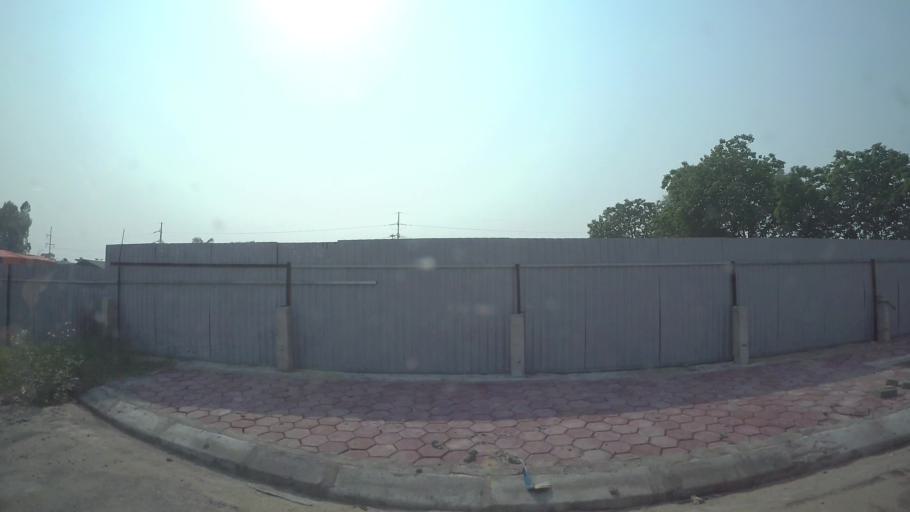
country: VN
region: Ha Noi
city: Ha Dong
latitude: 20.9526
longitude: 105.7888
